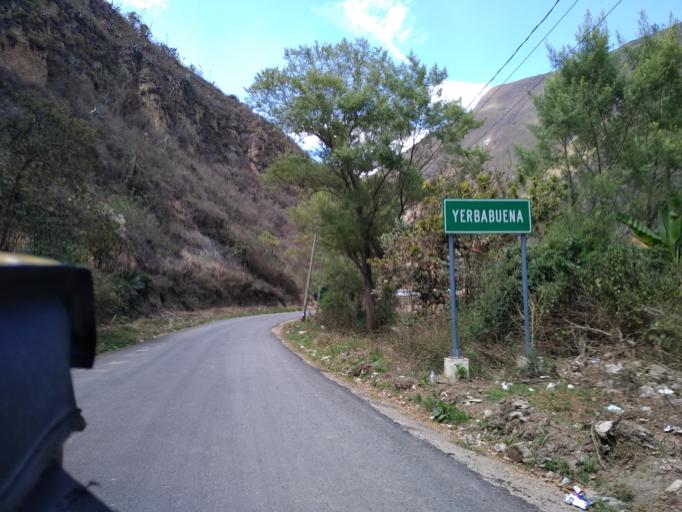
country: PE
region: Amazonas
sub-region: Provincia de Chachapoyas
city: Duraznopampa
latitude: -6.5628
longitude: -77.8299
